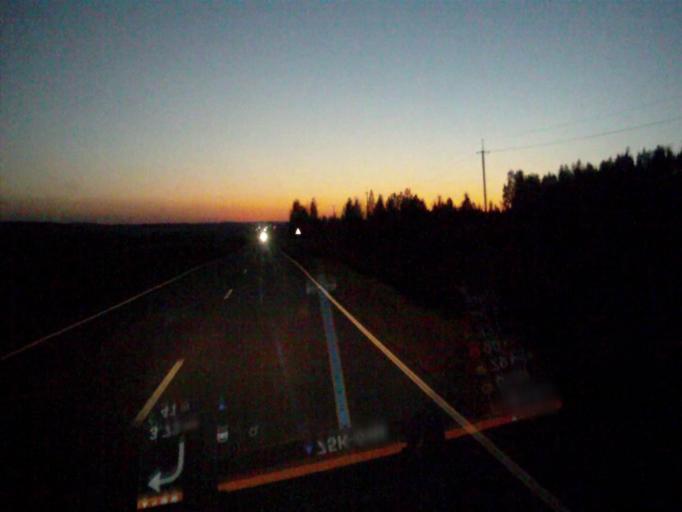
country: RU
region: Chelyabinsk
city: Chebarkul'
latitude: 55.2205
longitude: 60.5069
